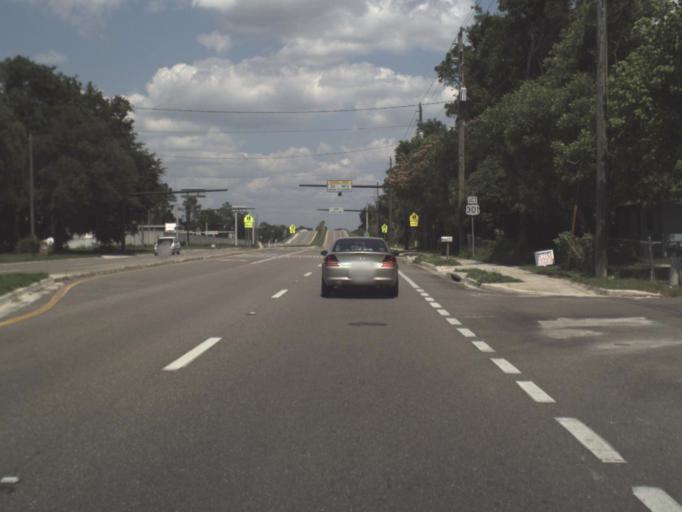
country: US
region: Florida
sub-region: Alachua County
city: Hawthorne
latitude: 29.5961
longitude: -82.0944
